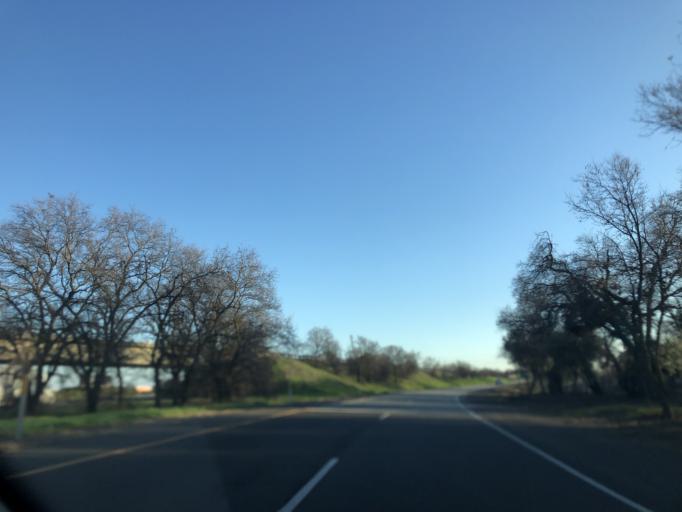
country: US
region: California
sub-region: Yolo County
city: Woodland
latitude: 38.6846
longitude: -121.7516
